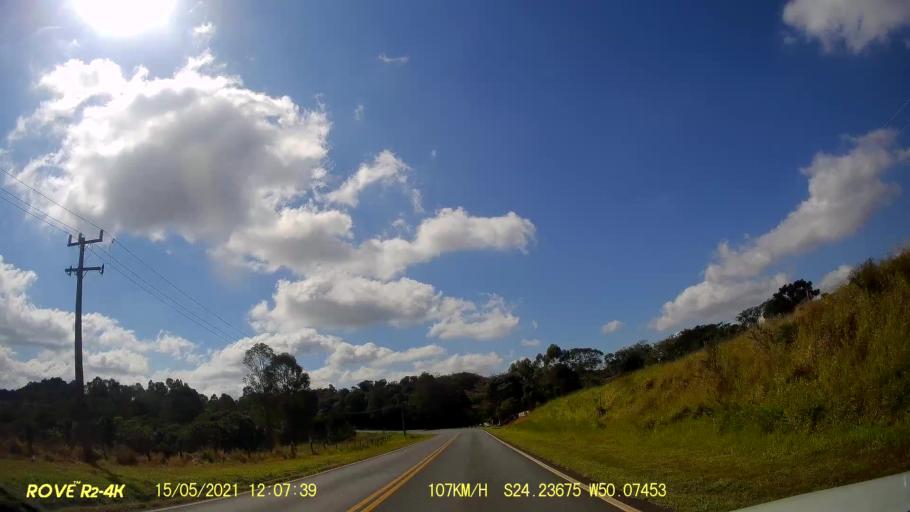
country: BR
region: Parana
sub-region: Pirai Do Sul
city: Pirai do Sul
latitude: -24.2367
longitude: -50.0744
